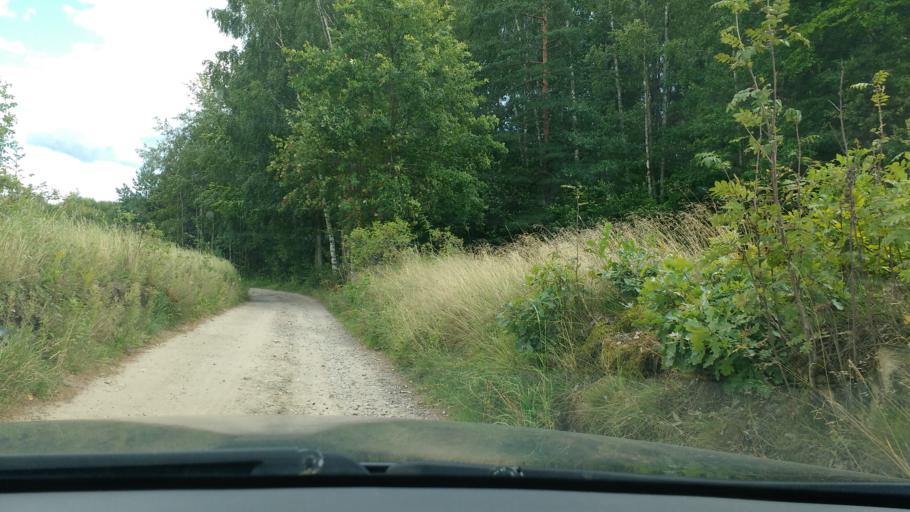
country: PL
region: Pomeranian Voivodeship
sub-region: Powiat kartuski
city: Chwaszczyno
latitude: 54.4743
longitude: 18.4350
